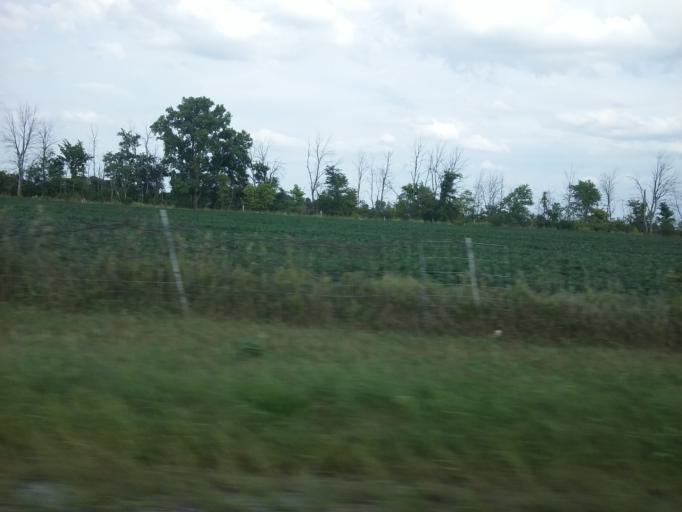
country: US
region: Ohio
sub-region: Wood County
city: Bowling Green
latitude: 41.2910
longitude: -83.6502
